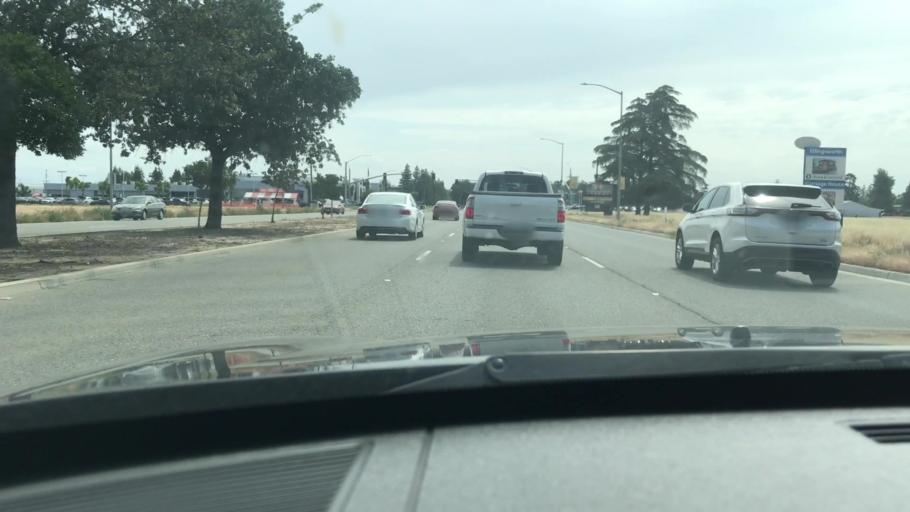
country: US
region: California
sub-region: Fresno County
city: Clovis
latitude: 36.8375
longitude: -119.7223
